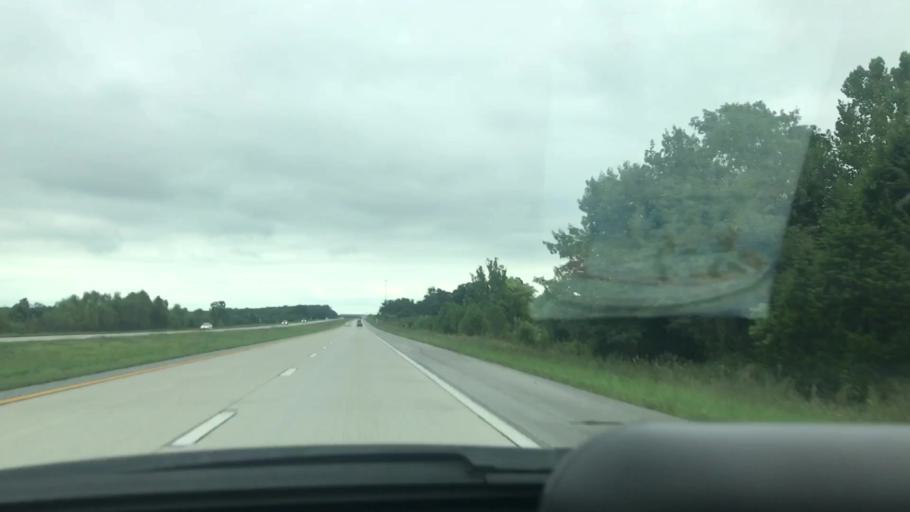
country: US
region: Missouri
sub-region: Greene County
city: Fair Grove
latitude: 37.4918
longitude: -93.1391
